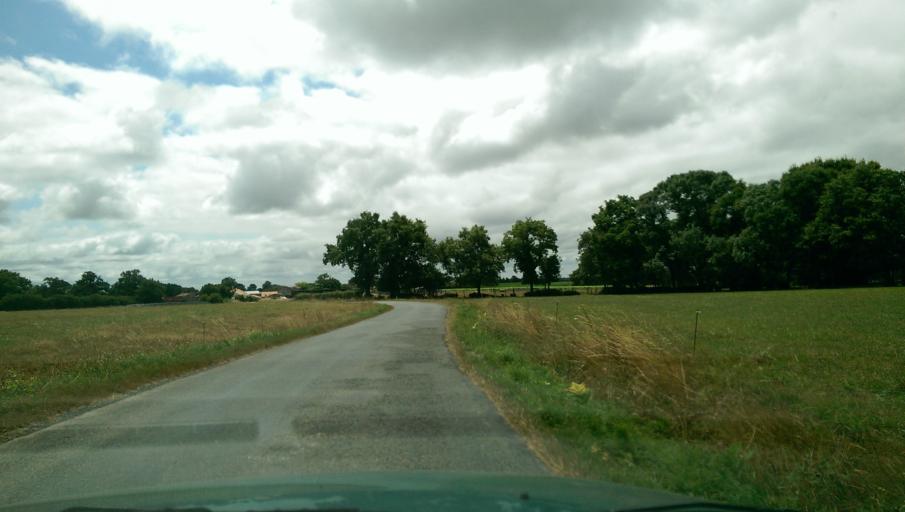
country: FR
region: Pays de la Loire
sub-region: Departement de la Loire-Atlantique
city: Remouille
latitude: 47.0676
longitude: -1.3625
